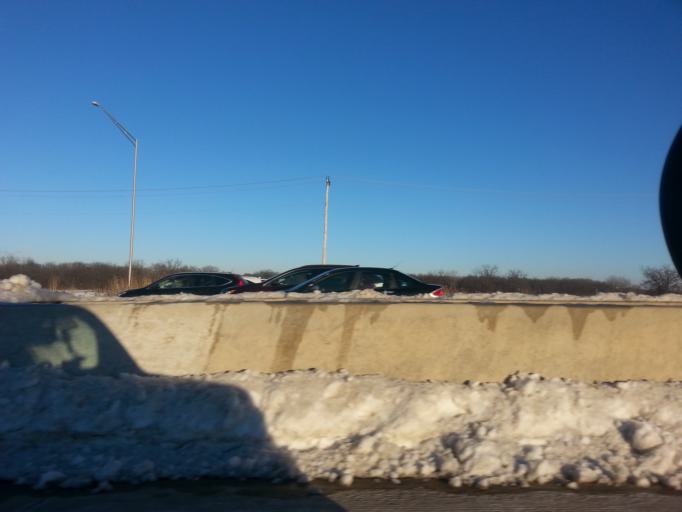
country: US
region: Wisconsin
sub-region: Kenosha County
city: Pleasant Prairie
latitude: 42.4957
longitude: -87.9505
